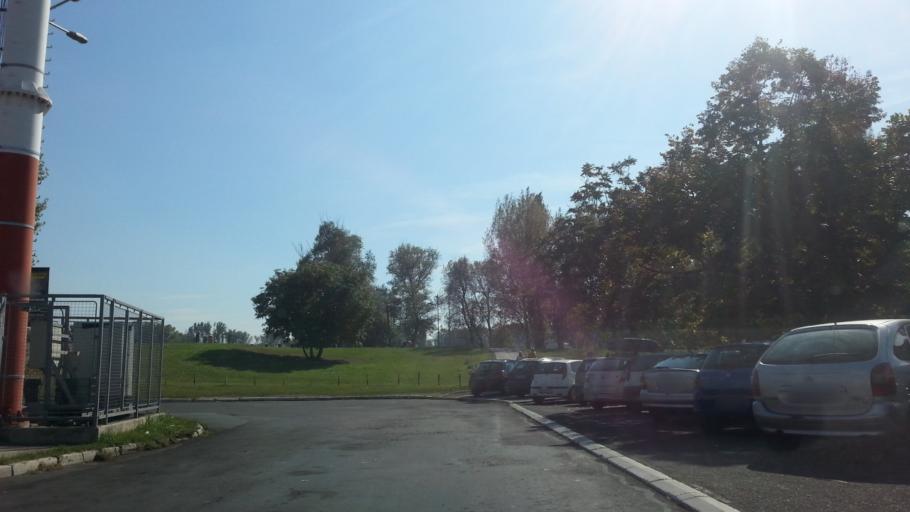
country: RS
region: Central Serbia
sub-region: Belgrade
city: Cukarica
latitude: 44.7975
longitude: 20.4002
